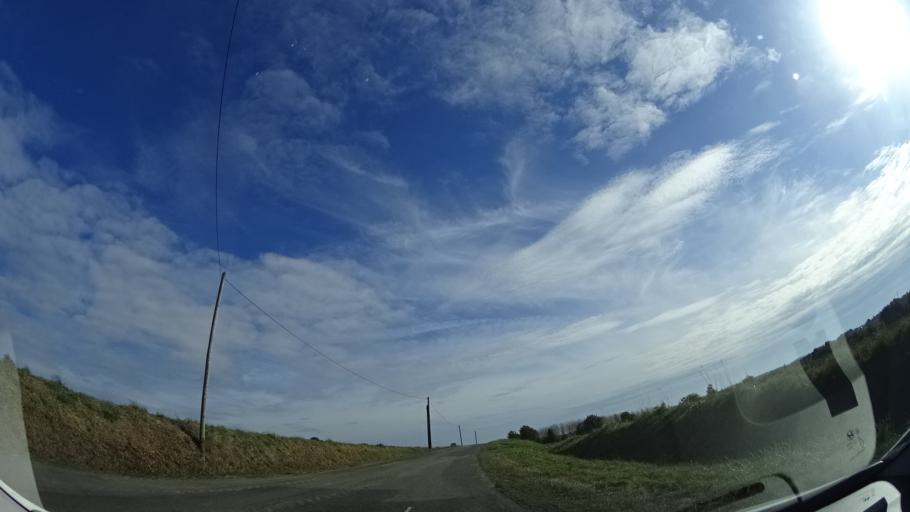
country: FR
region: Brittany
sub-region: Departement d'Ille-et-Vilaine
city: Geveze
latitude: 48.2370
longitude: -1.8061
